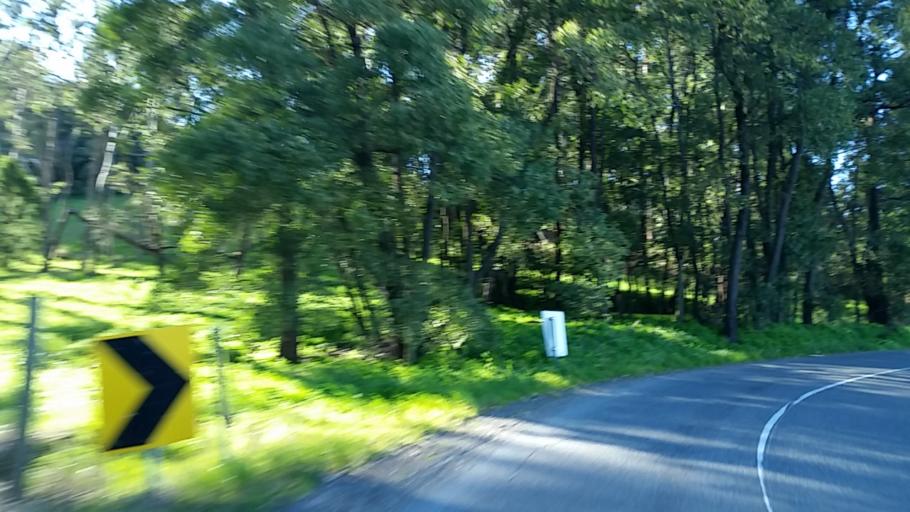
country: AU
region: South Australia
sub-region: Adelaide Hills
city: Adelaide Hills
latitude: -34.9477
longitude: 138.7224
